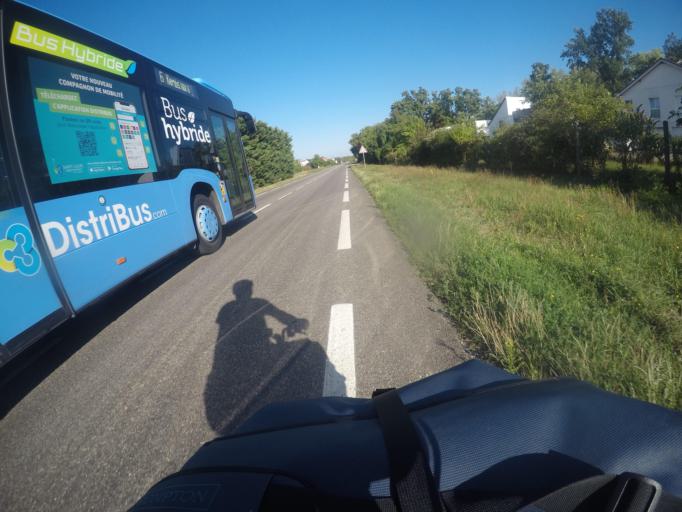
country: FR
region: Alsace
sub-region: Departement du Haut-Rhin
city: Kembs
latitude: 47.6622
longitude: 7.5026
